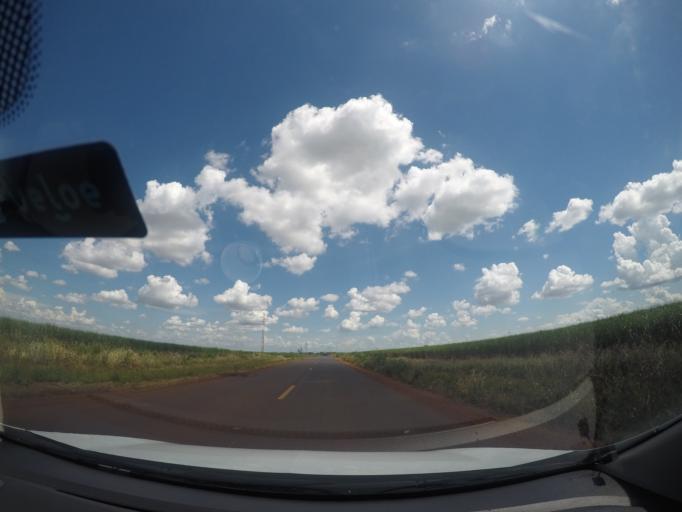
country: BR
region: Minas Gerais
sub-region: Frutal
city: Frutal
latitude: -19.8237
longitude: -48.7326
